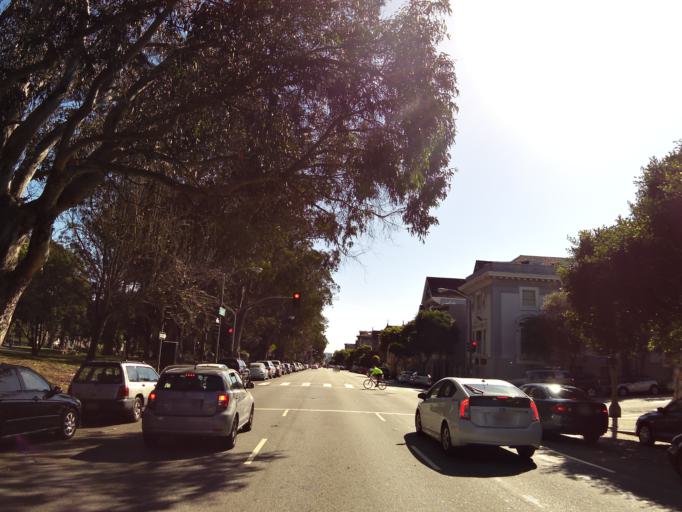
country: US
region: California
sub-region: San Francisco County
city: San Francisco
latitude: 37.7717
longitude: -122.4493
